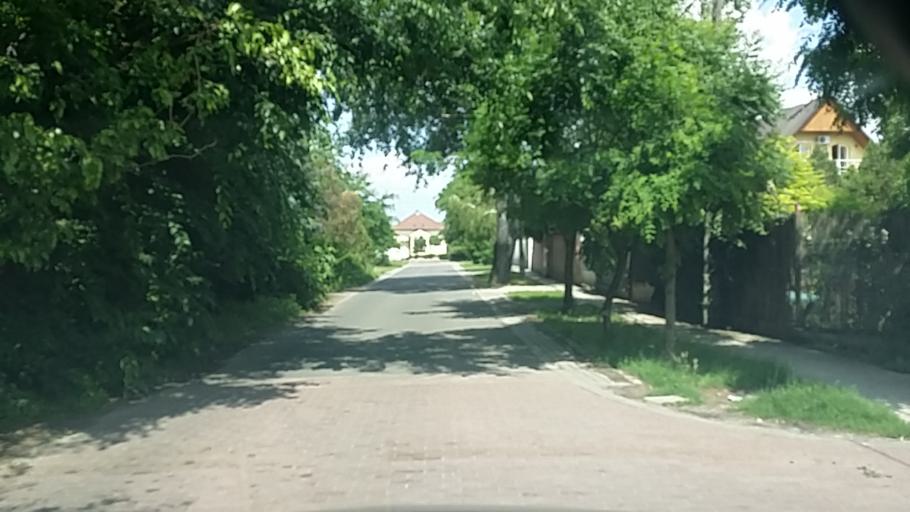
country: HU
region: Budapest
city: Budapest XVI. keruelet
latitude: 47.5209
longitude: 19.1470
